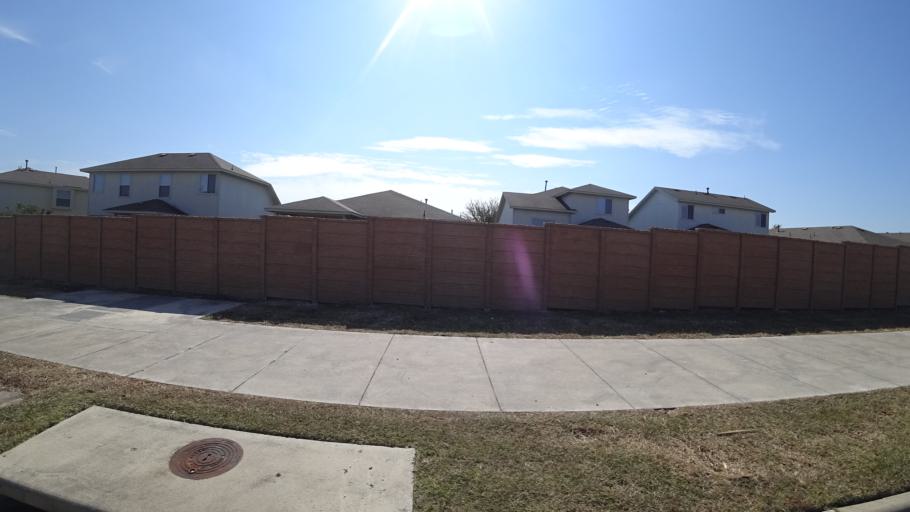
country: US
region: Texas
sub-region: Travis County
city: Pflugerville
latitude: 30.4294
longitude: -97.6383
